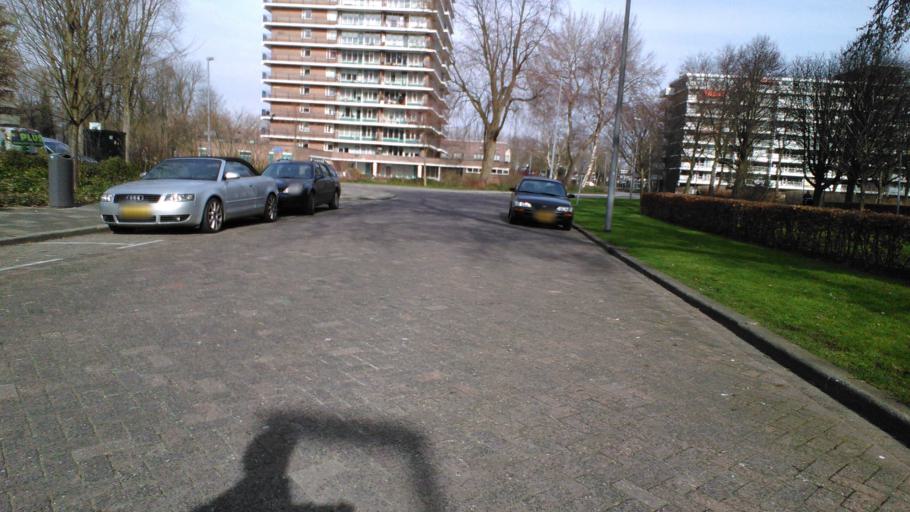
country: NL
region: South Holland
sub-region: Gemeente Rotterdam
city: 's-Gravenland
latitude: 51.9615
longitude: 4.5344
